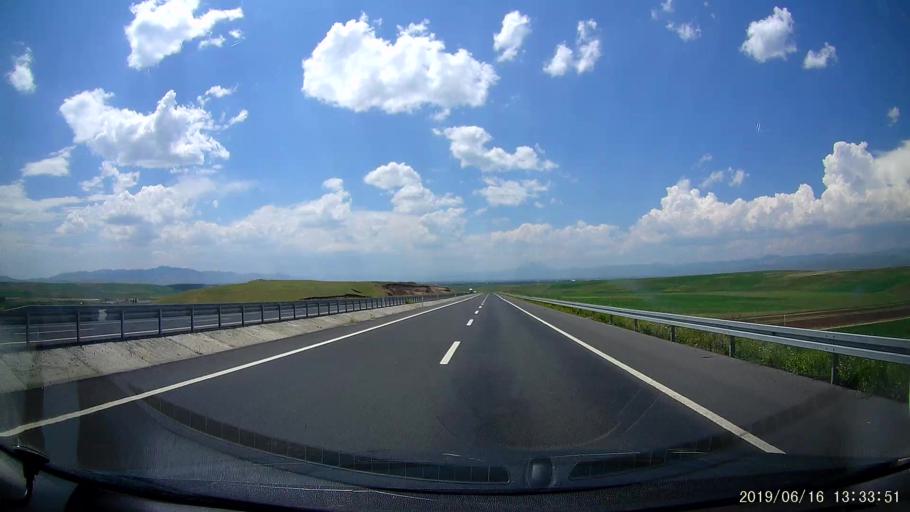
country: TR
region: Agri
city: Agri
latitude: 39.7091
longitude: 43.1434
